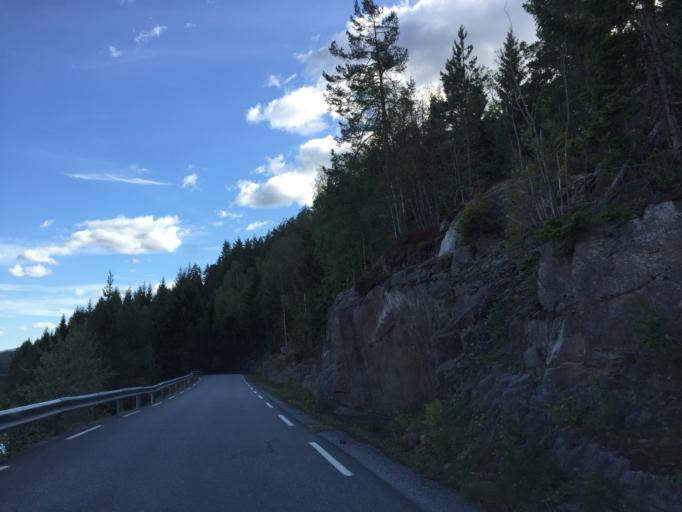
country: NO
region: Buskerud
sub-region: Ovre Eiker
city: Hokksund
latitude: 59.6528
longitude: 9.9148
